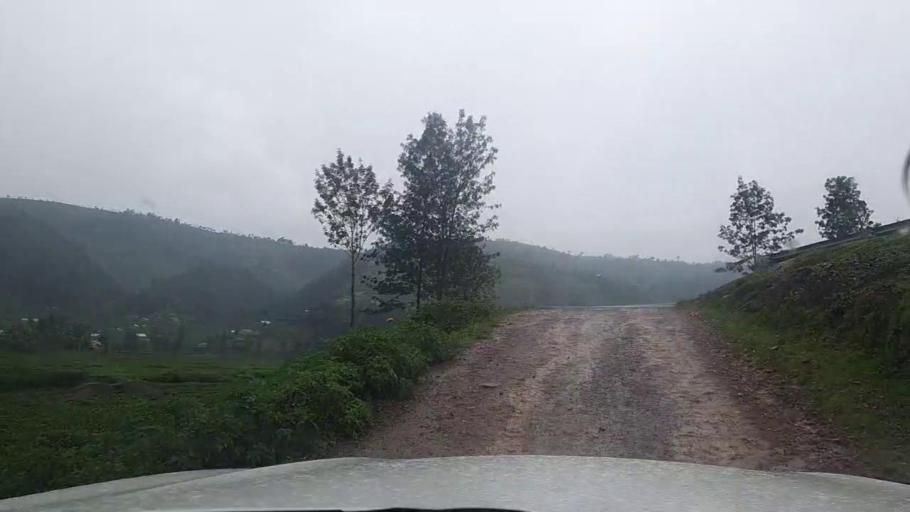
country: RW
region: Northern Province
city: Byumba
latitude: -1.6535
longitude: 29.9132
